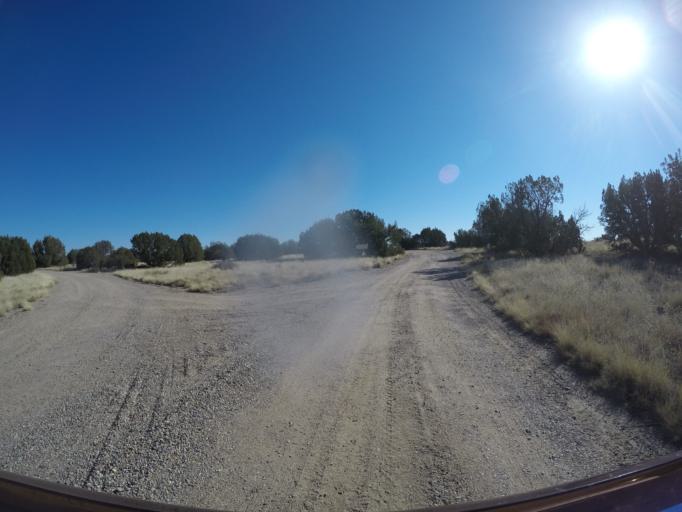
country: US
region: Colorado
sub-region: Otero County
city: La Junta
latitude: 37.6596
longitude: -103.5724
